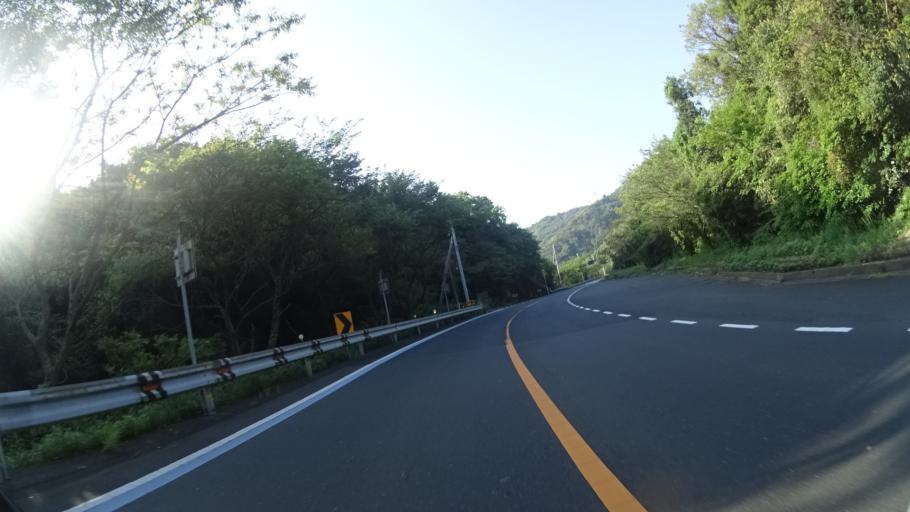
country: JP
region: Ehime
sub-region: Nishiuwa-gun
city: Ikata-cho
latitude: 33.4581
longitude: 132.2743
